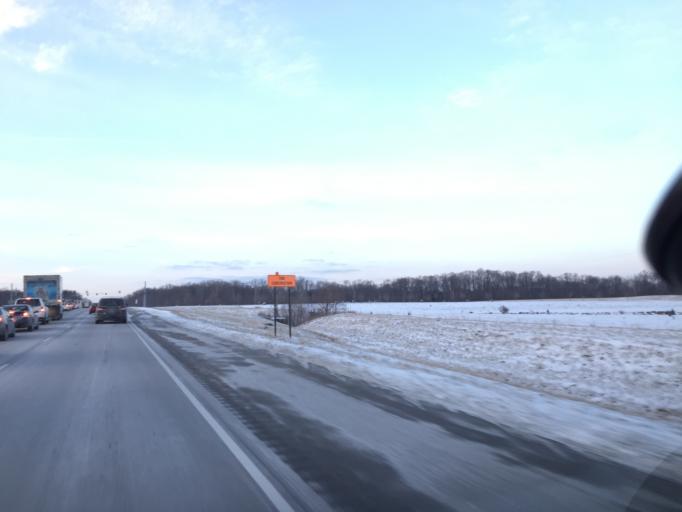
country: US
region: Indiana
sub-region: Monroe County
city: Bloomington
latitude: 39.1915
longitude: -86.5698
